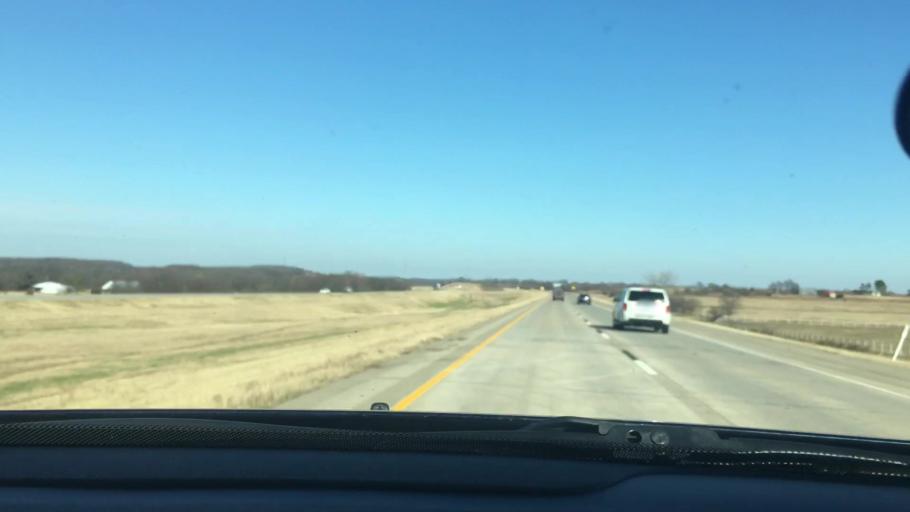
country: US
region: Oklahoma
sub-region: Love County
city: Marietta
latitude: 33.9705
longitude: -97.1340
